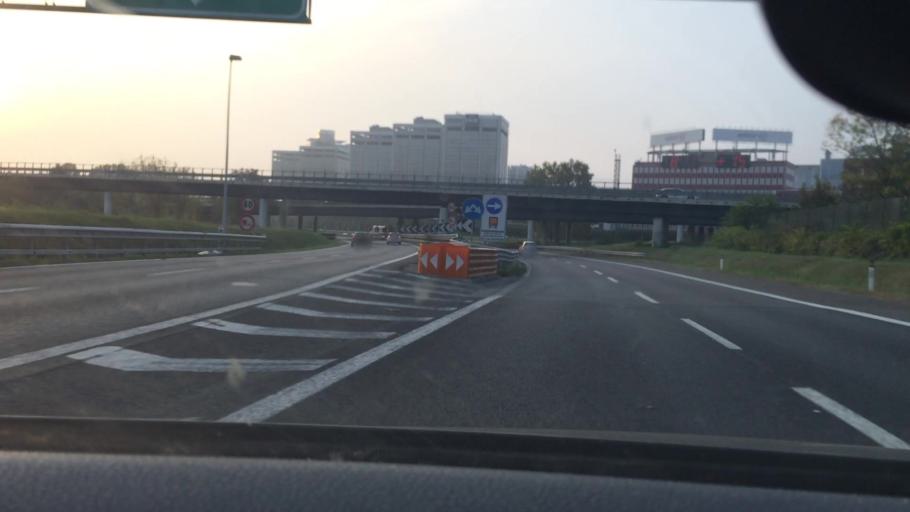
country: IT
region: Lombardy
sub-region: Citta metropolitana di Milano
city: Baranzate
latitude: 45.5167
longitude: 9.1165
